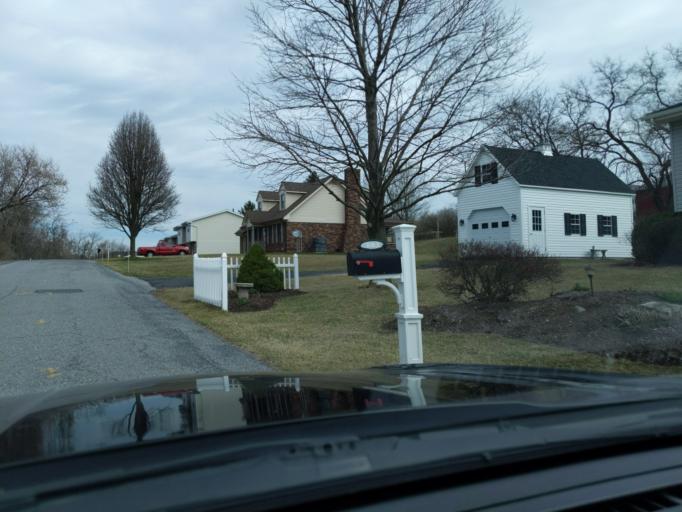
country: US
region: Pennsylvania
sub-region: Blair County
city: Greenwood
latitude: 40.5262
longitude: -78.3714
